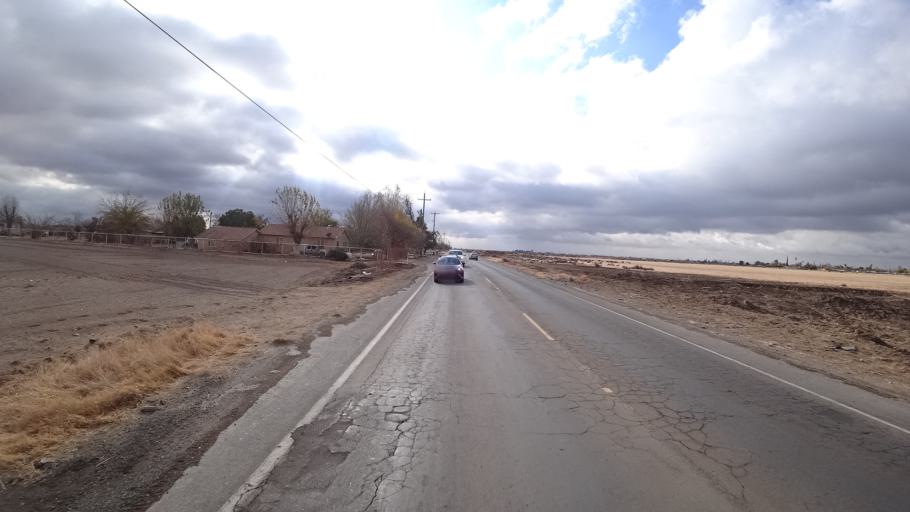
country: US
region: California
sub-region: Kern County
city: Greenfield
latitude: 35.3060
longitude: -118.9854
